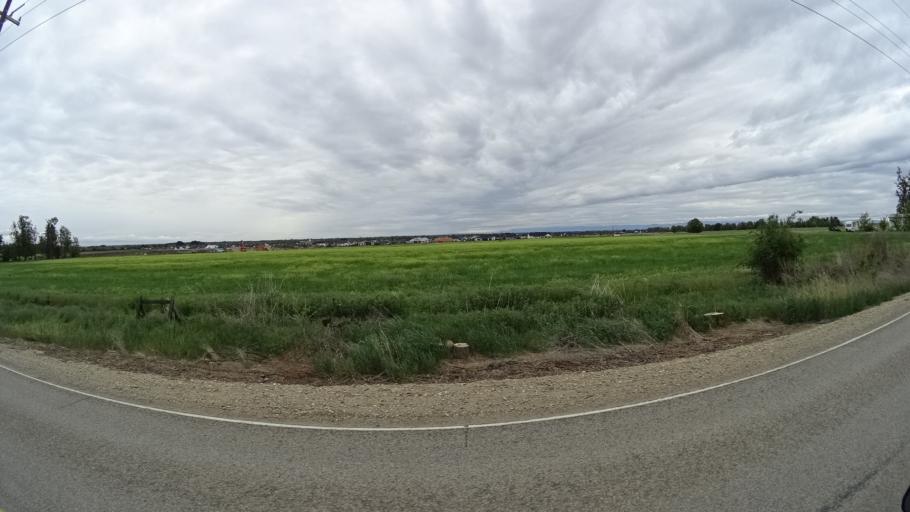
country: US
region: Idaho
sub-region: Ada County
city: Star
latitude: 43.7210
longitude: -116.4262
